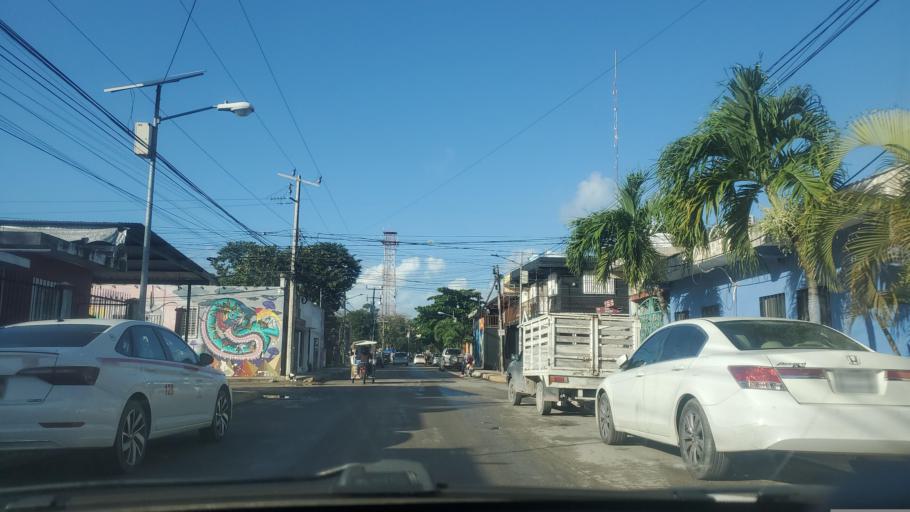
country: MX
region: Quintana Roo
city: Tulum
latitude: 20.2102
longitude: -87.4610
